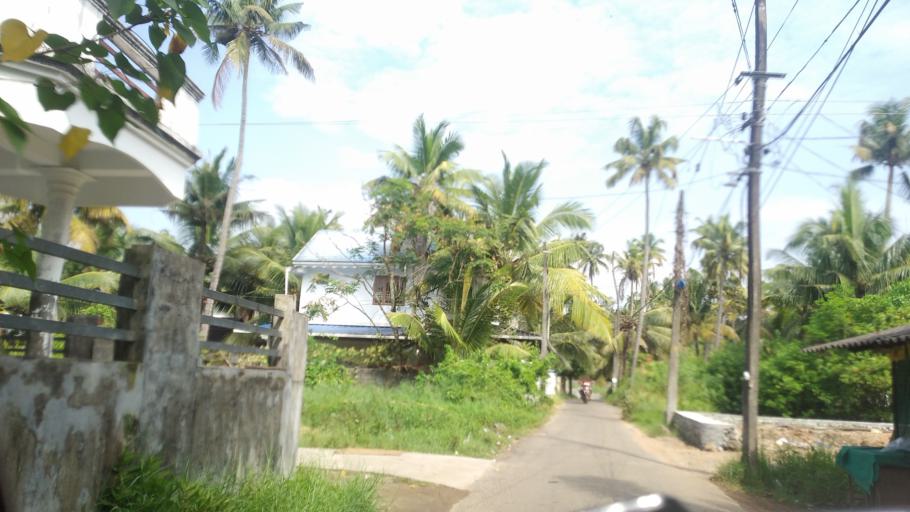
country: IN
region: Kerala
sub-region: Ernakulam
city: Elur
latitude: 10.0881
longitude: 76.2022
